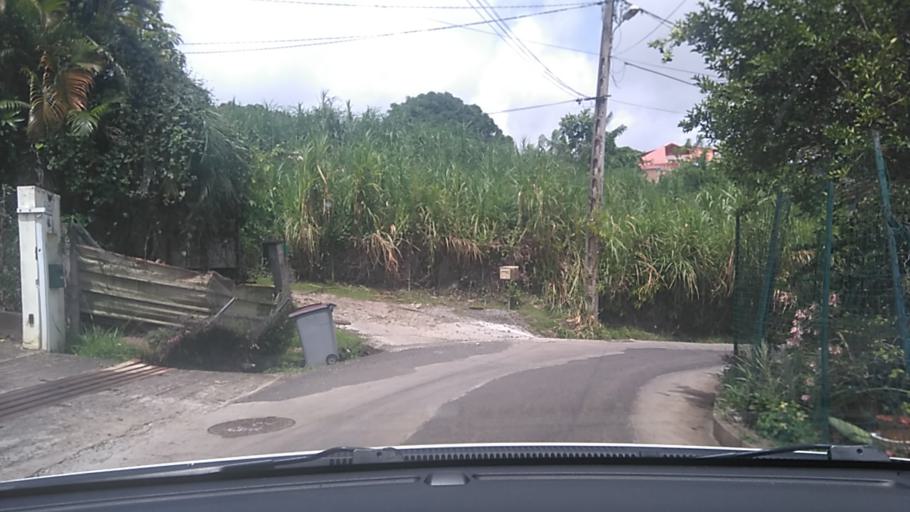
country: MQ
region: Martinique
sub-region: Martinique
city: Saint-Esprit
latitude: 14.5639
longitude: -60.9319
